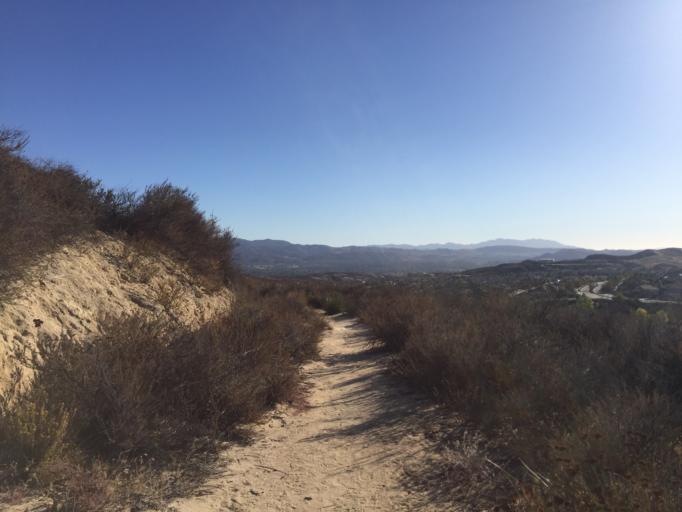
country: US
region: California
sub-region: Ventura County
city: Simi Valley
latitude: 34.3044
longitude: -118.7538
